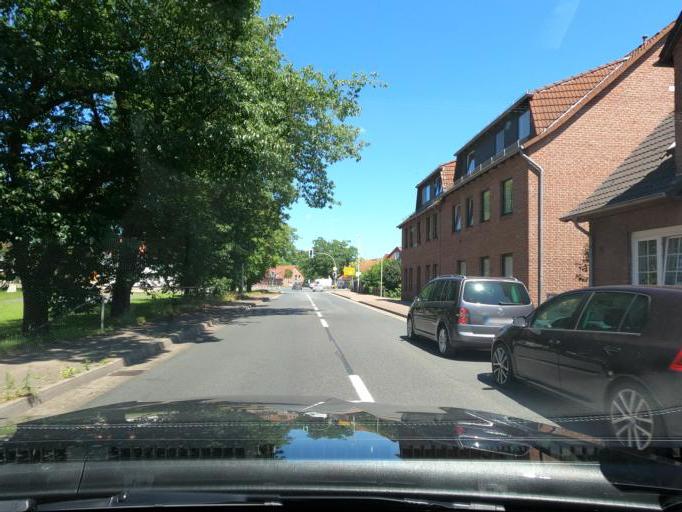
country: DE
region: Lower Saxony
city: Lehrte
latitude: 52.4008
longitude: 9.9745
